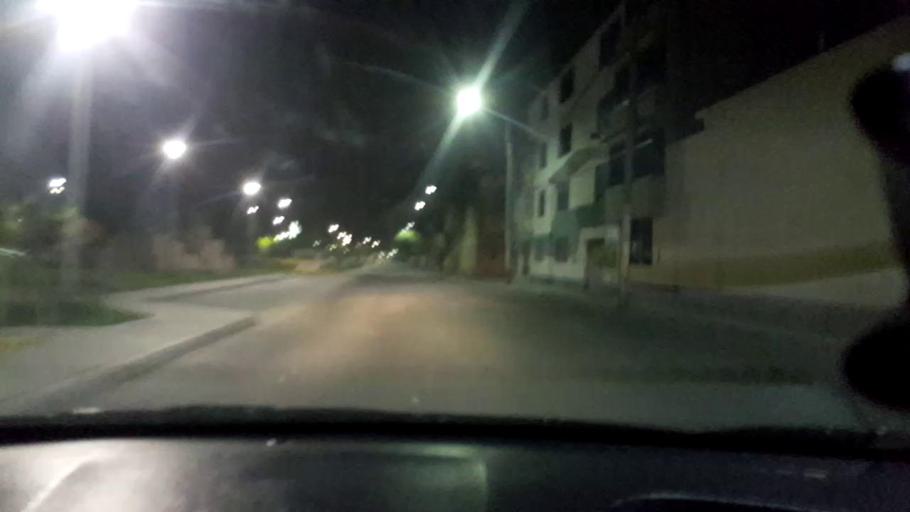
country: PE
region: Lambayeque
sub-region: Provincia de Chiclayo
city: Chiclayo
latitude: -6.7844
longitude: -79.8343
